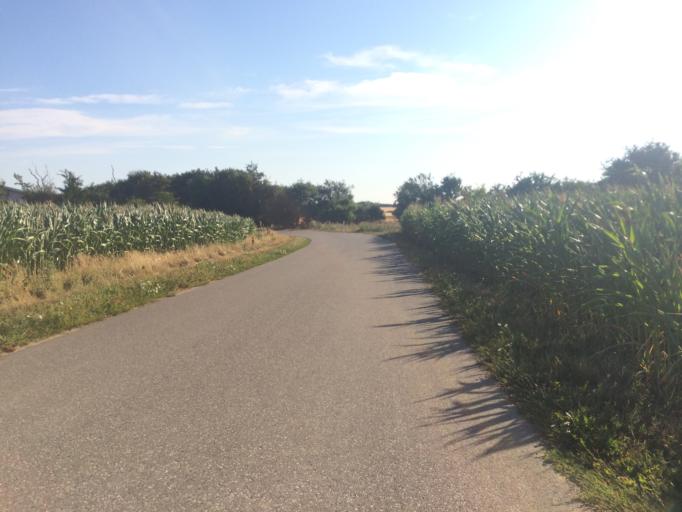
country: DK
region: Central Jutland
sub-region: Holstebro Kommune
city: Vinderup
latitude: 56.6091
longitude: 8.7734
